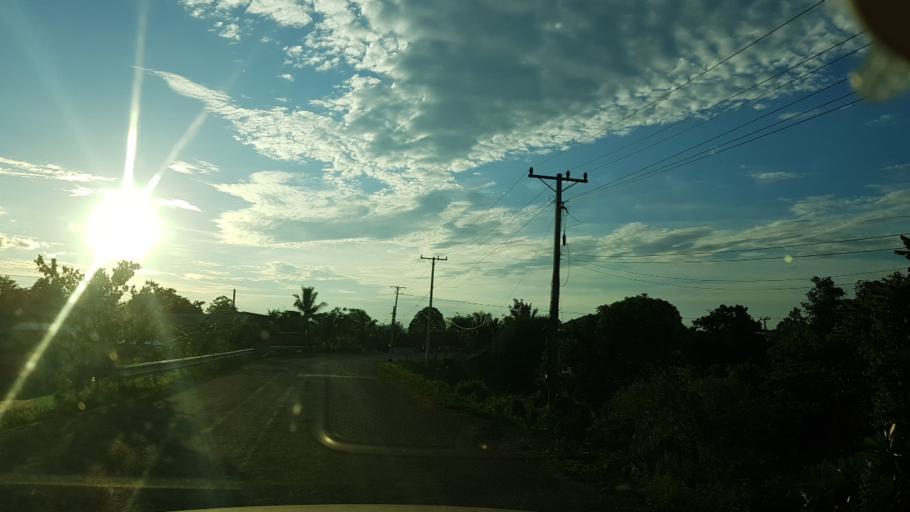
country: TH
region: Nong Khai
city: Sangkhom
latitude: 18.0932
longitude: 102.2874
